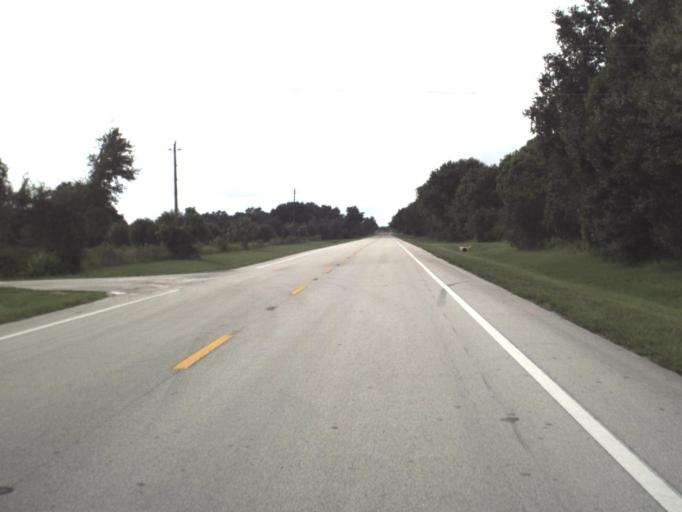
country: US
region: Florida
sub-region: DeSoto County
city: Nocatee
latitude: 27.2016
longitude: -81.9483
